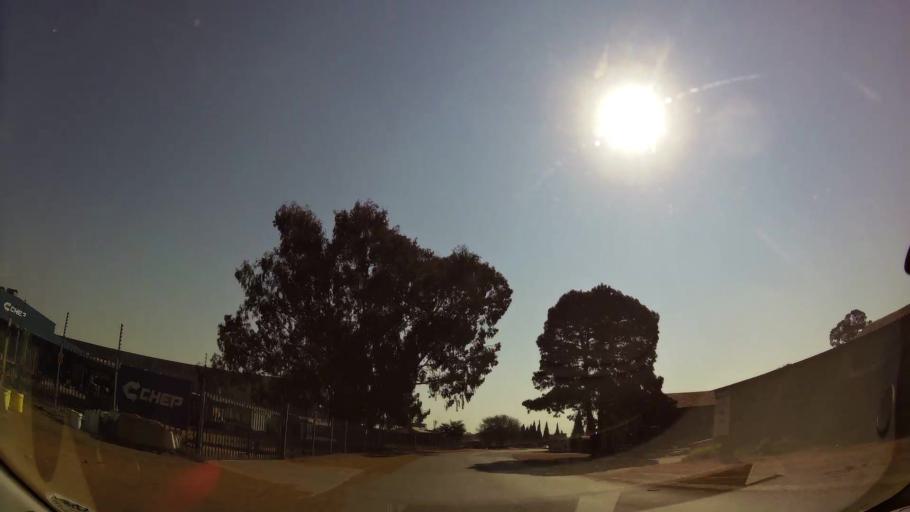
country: ZA
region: Gauteng
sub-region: Ekurhuleni Metropolitan Municipality
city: Boksburg
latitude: -26.1723
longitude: 28.2116
